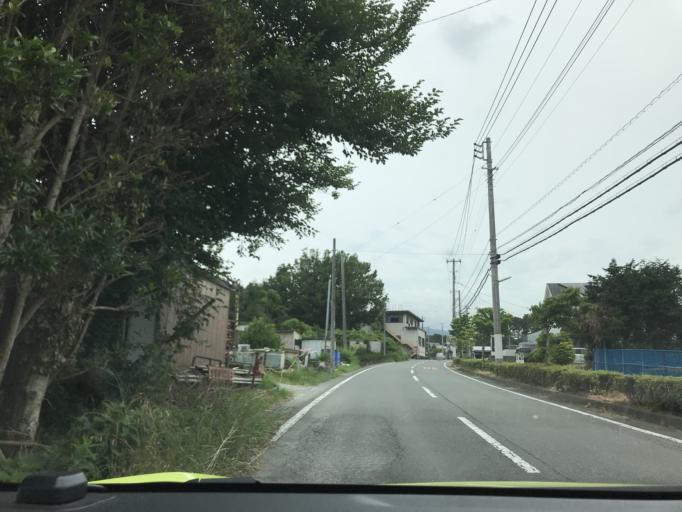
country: JP
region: Shizuoka
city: Numazu
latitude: 35.1353
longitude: 138.8579
